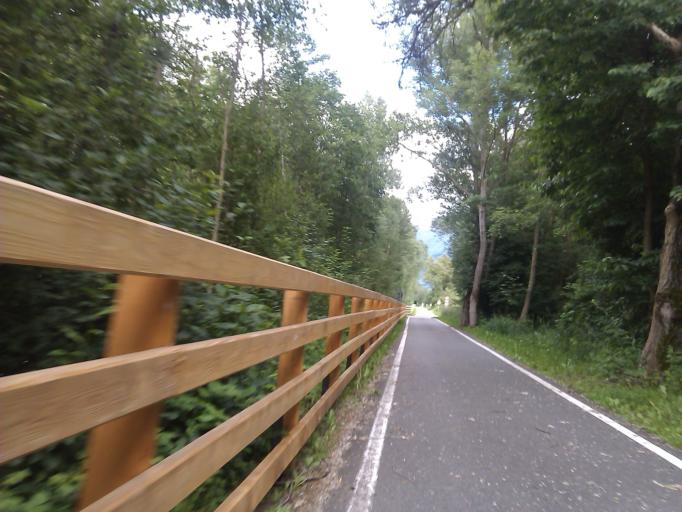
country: IT
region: Trentino-Alto Adige
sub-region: Bolzano
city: Prato Allo Stelvio
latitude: 46.6418
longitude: 10.5897
